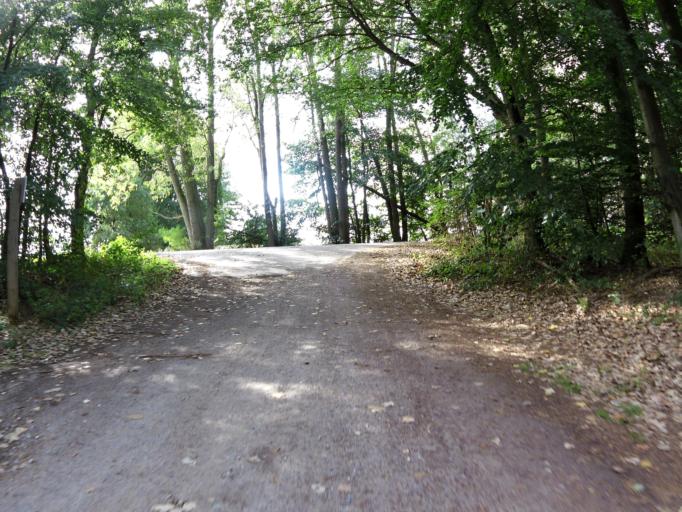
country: DE
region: Mecklenburg-Vorpommern
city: Seebad Bansin
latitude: 53.9461
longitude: 14.0993
